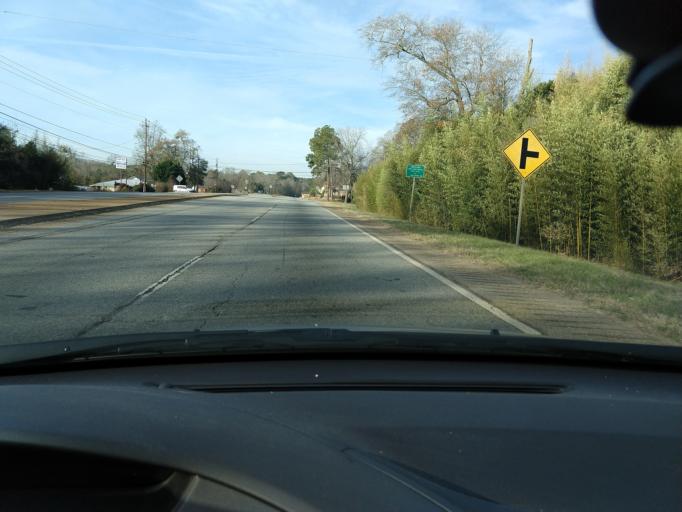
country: US
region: Georgia
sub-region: Sumter County
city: Americus
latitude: 32.0632
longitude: -84.2597
